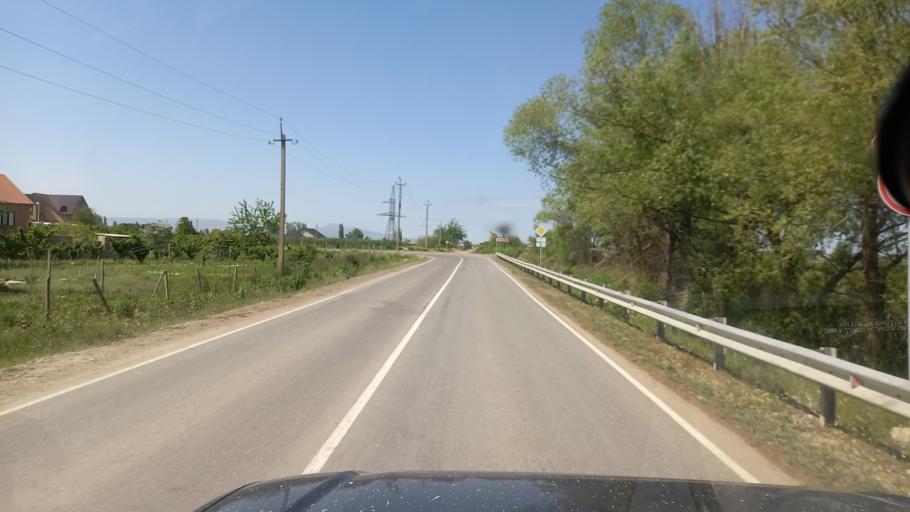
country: RU
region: Dagestan
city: Novaya Maka
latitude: 41.8236
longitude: 48.3999
